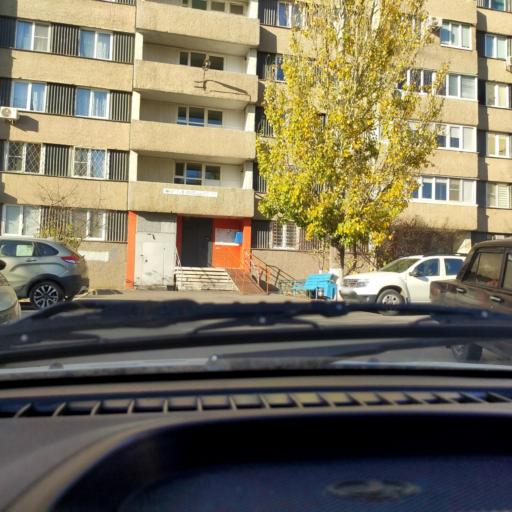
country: RU
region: Samara
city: Zhigulevsk
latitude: 53.4732
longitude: 49.4693
